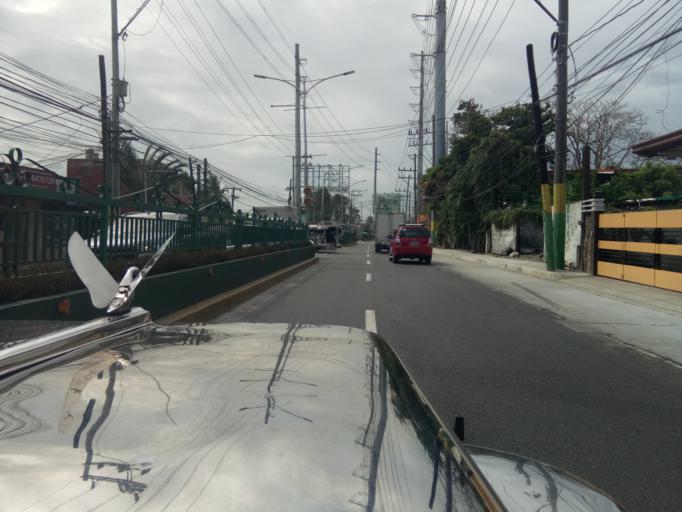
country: PH
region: Calabarzon
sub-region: Province of Cavite
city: Dasmarinas
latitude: 14.3164
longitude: 120.9441
